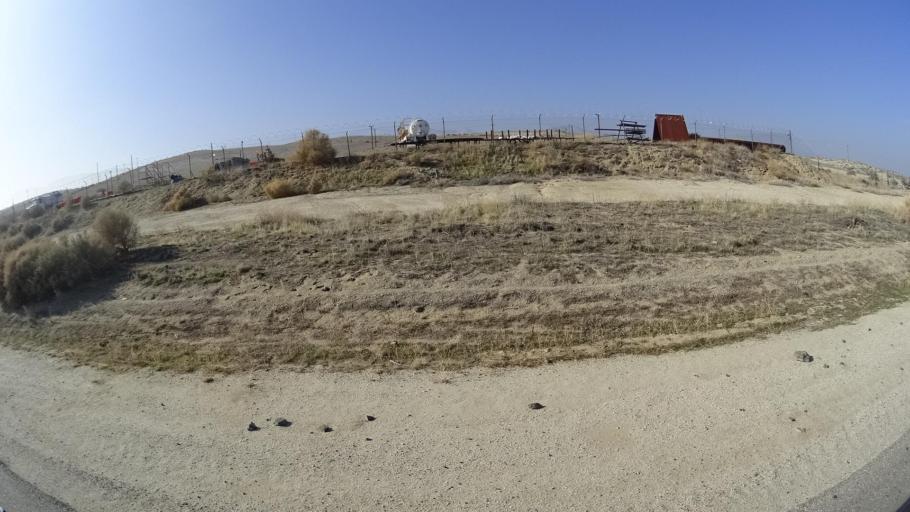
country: US
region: California
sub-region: Kern County
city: Taft Heights
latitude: 35.1689
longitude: -119.5336
